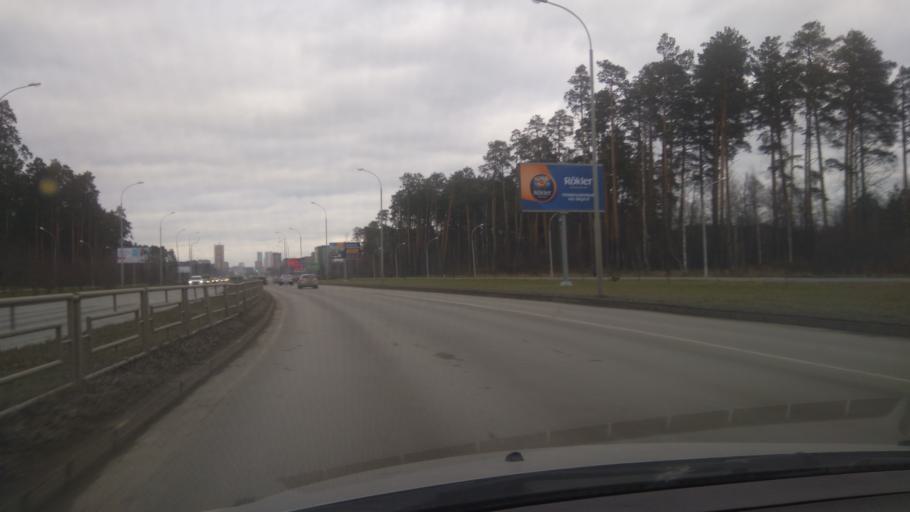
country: RU
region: Sverdlovsk
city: Sovkhoznyy
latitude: 56.7995
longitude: 60.5332
